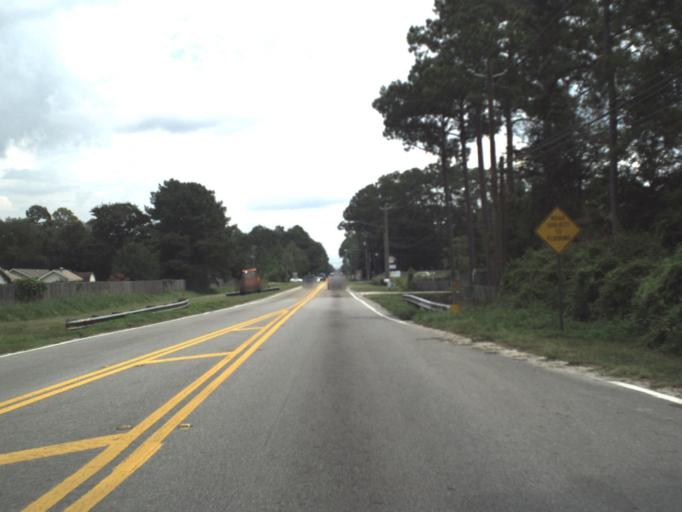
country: US
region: Florida
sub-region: Bay County
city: Lynn Haven
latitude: 30.2332
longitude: -85.6180
